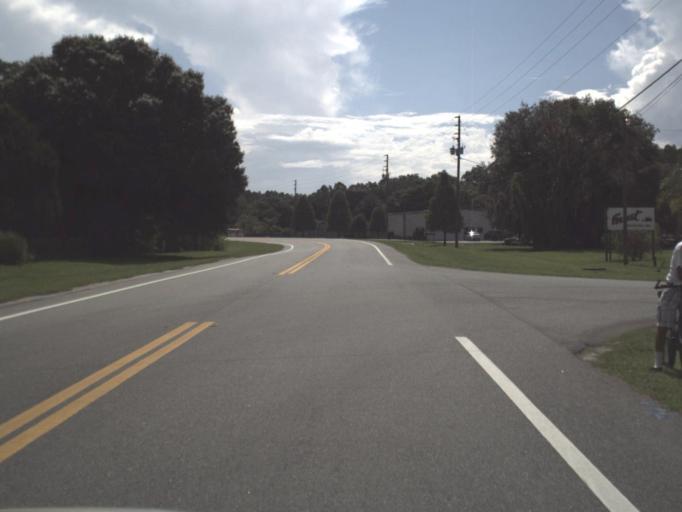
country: US
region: Florida
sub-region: Pasco County
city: Odessa
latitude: 28.1899
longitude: -82.5781
